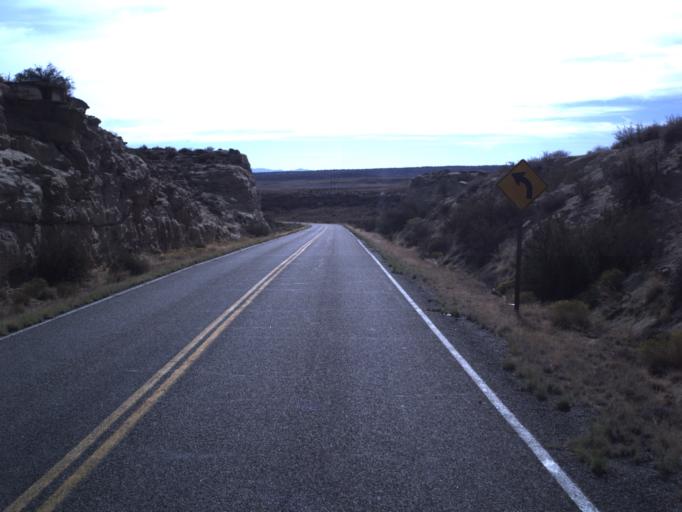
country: US
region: Utah
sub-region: San Juan County
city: Blanding
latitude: 37.4192
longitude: -109.4561
